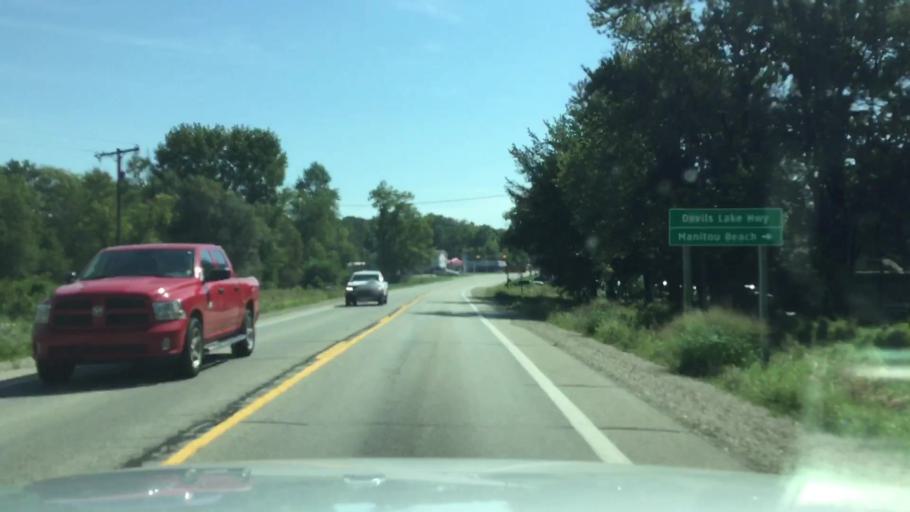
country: US
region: Michigan
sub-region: Lenawee County
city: Manitou Beach-Devils Lake
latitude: 42.0087
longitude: -84.2956
